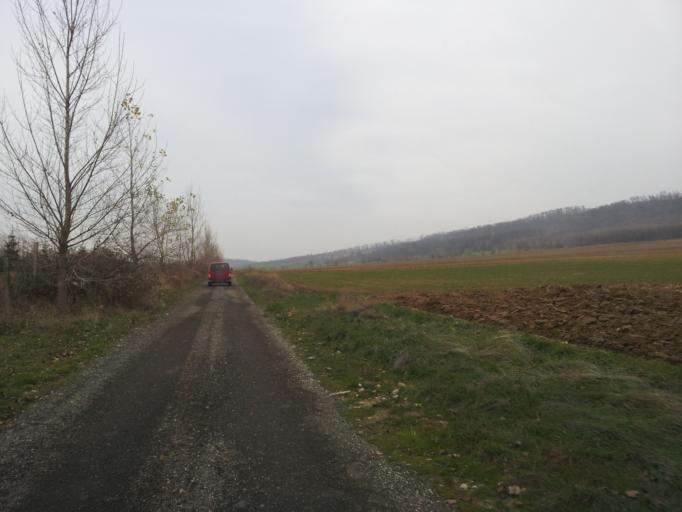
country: HU
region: Zala
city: Cserszegtomaj
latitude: 46.8411
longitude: 17.2317
